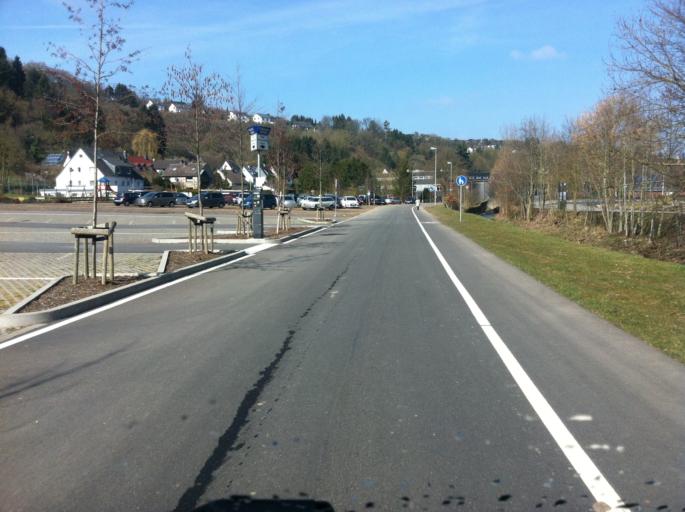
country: DE
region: North Rhine-Westphalia
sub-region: Regierungsbezirk Koln
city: Bad Munstereifel
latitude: 50.5472
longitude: 6.7638
